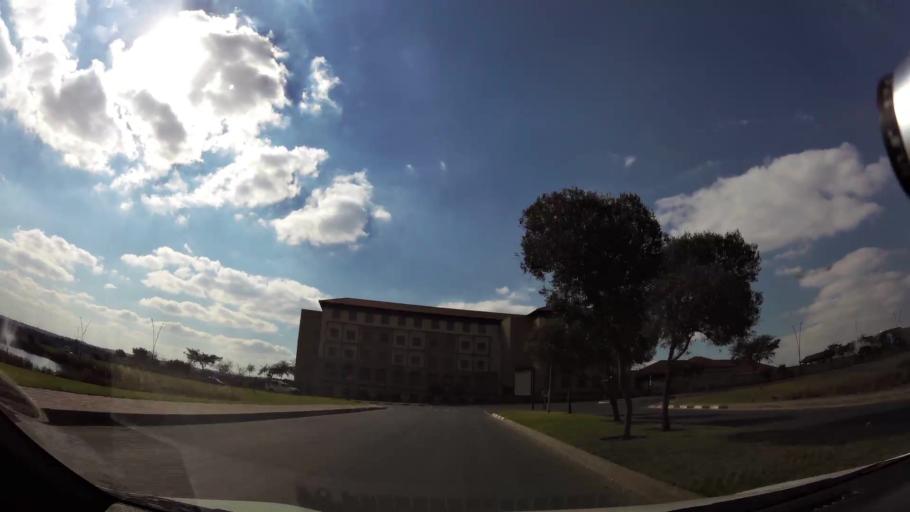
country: ZA
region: Gauteng
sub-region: City of Johannesburg Metropolitan Municipality
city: Midrand
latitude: -26.0152
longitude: 28.1002
